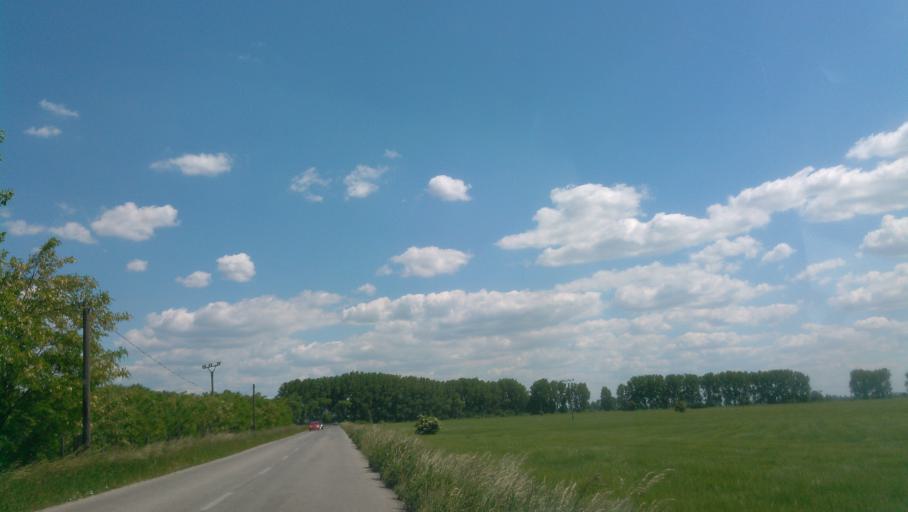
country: SK
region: Trnavsky
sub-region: Okres Dunajska Streda
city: Velky Meder
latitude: 47.9071
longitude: 17.8632
